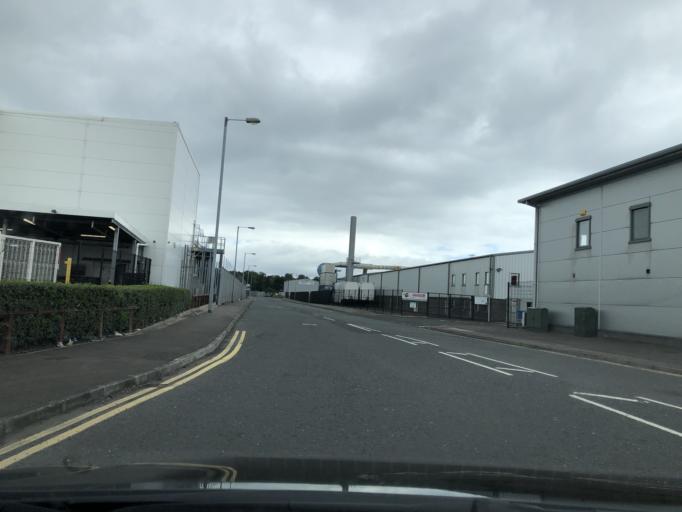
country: GB
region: Northern Ireland
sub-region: Larne District
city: Larne
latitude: 54.8460
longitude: -5.8075
